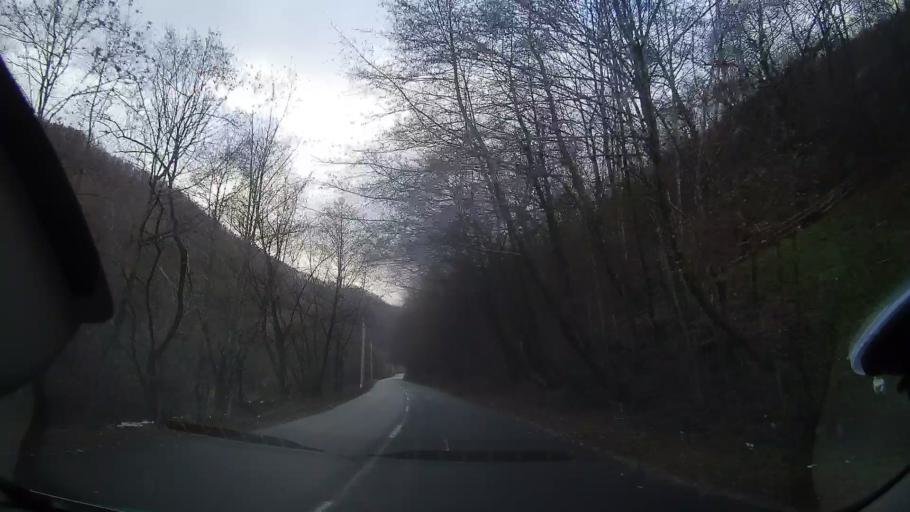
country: RO
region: Cluj
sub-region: Comuna Maguri-Racatau
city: Maguri-Racatau
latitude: 46.6770
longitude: 23.2575
